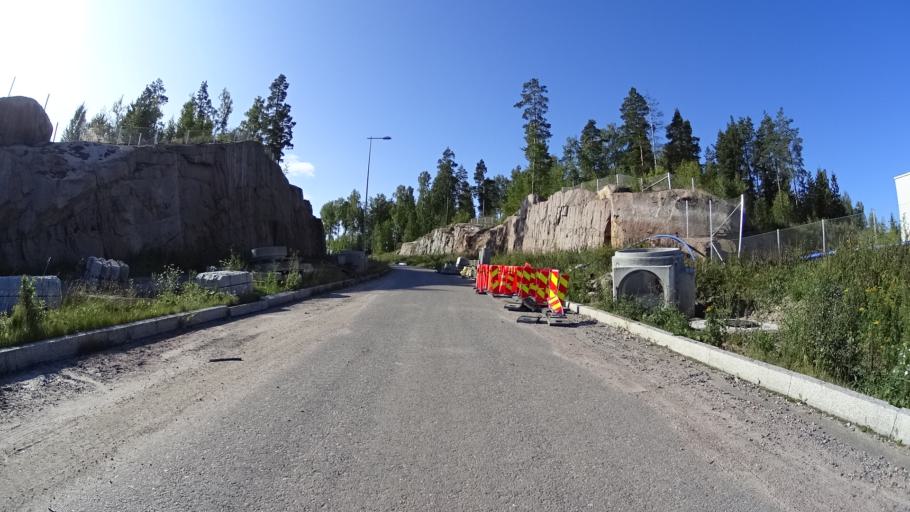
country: FI
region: Uusimaa
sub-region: Helsinki
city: Kilo
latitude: 60.2990
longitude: 24.7671
